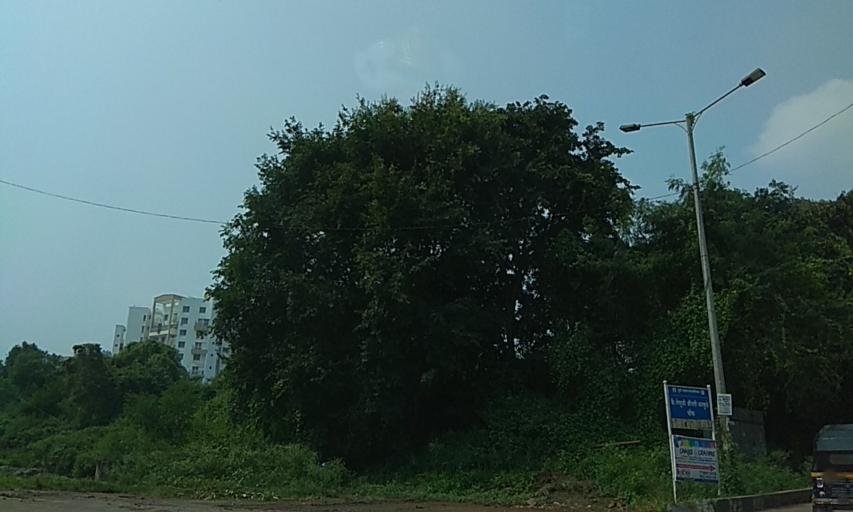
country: IN
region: Maharashtra
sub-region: Pune Division
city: Khadki
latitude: 18.5595
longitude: 73.7856
